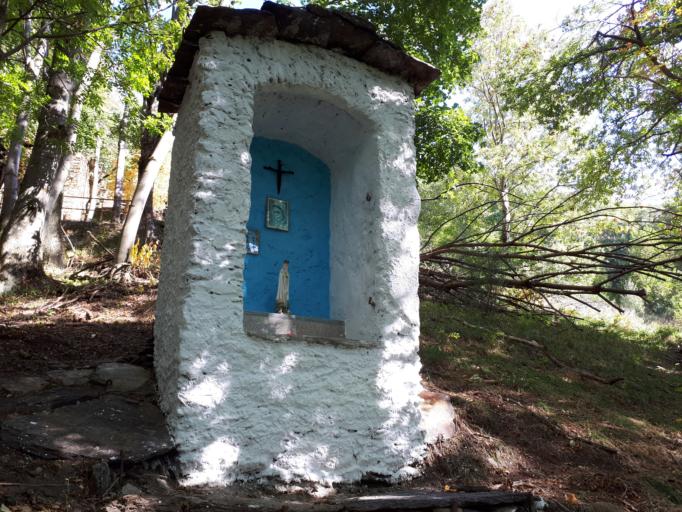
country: IT
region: Lombardy
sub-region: Provincia di Lecco
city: Vendrogno
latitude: 46.0542
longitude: 9.3334
